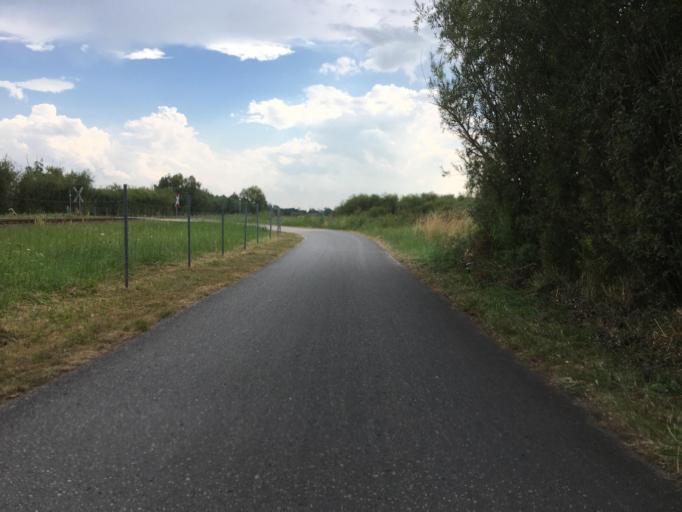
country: DE
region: Brandenburg
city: Zehdenick
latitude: 52.9936
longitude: 13.3205
